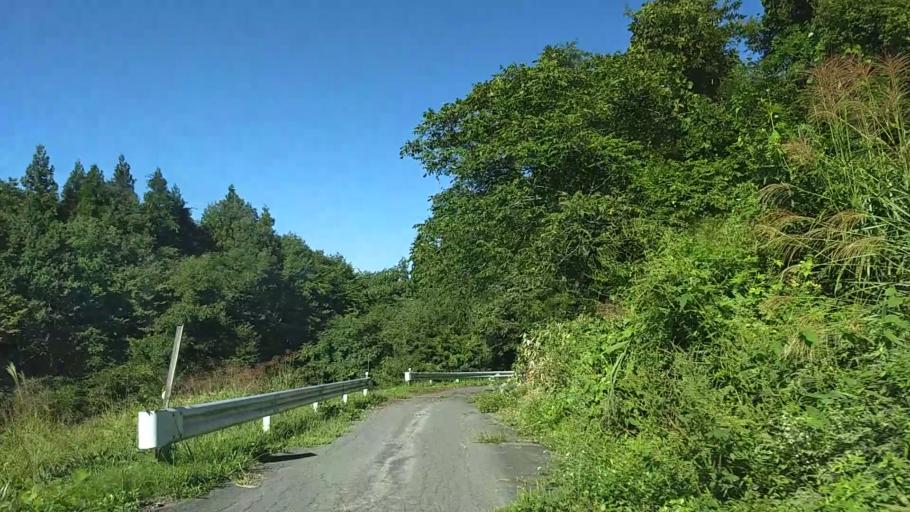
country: JP
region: Nagano
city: Nagano-shi
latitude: 36.5926
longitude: 138.0841
